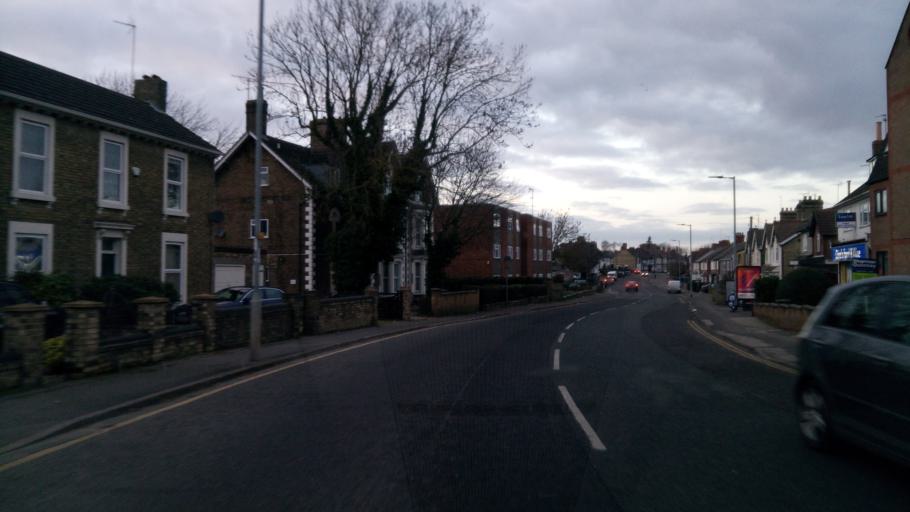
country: GB
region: England
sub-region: Peterborough
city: Peterborough
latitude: 52.5597
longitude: -0.2403
